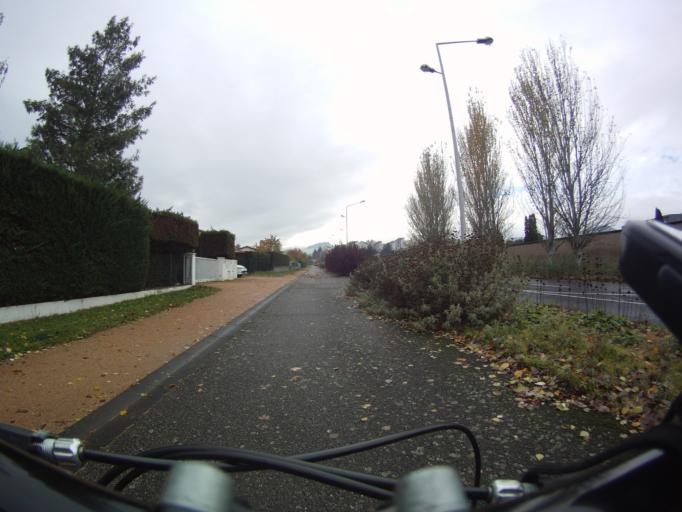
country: FR
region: Auvergne
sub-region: Departement du Puy-de-Dome
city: Aubiere
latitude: 45.7577
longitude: 3.1000
